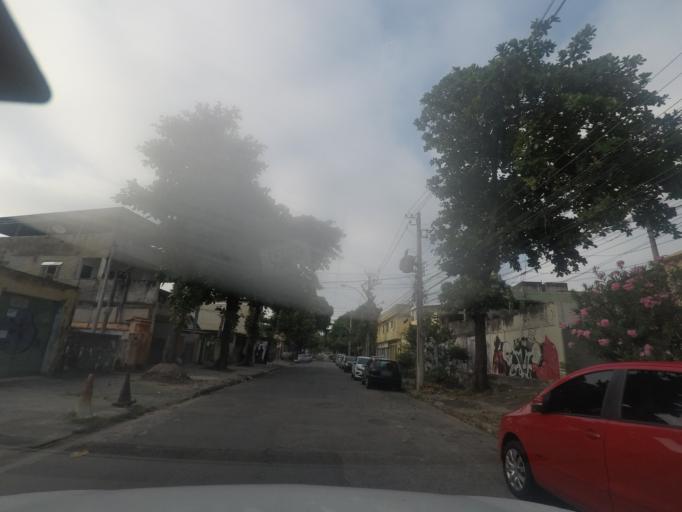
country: BR
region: Rio de Janeiro
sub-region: Duque De Caxias
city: Duque de Caxias
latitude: -22.8307
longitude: -43.2719
